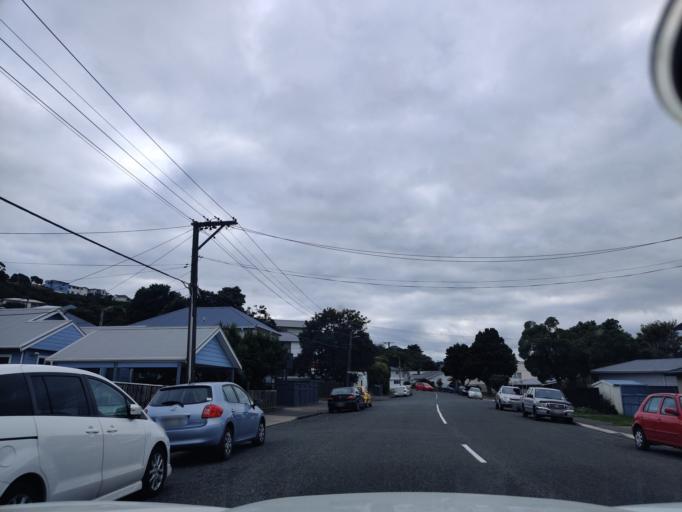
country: NZ
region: Wellington
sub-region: Wellington City
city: Wellington
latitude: -41.3117
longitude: 174.8162
